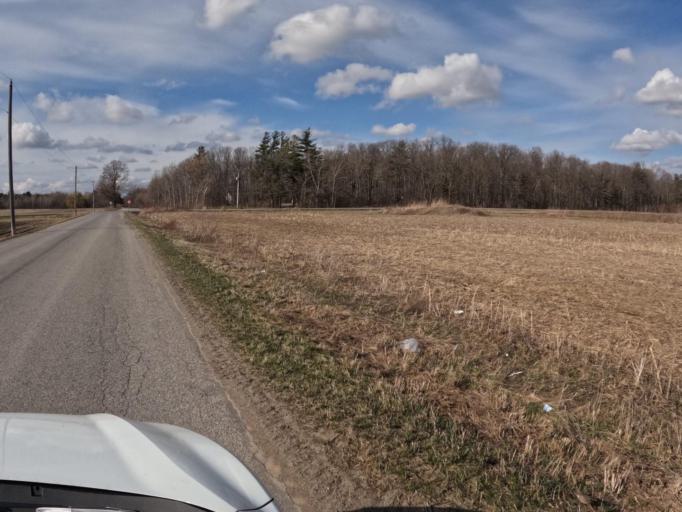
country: CA
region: Ontario
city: Norfolk County
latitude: 42.8862
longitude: -80.2839
